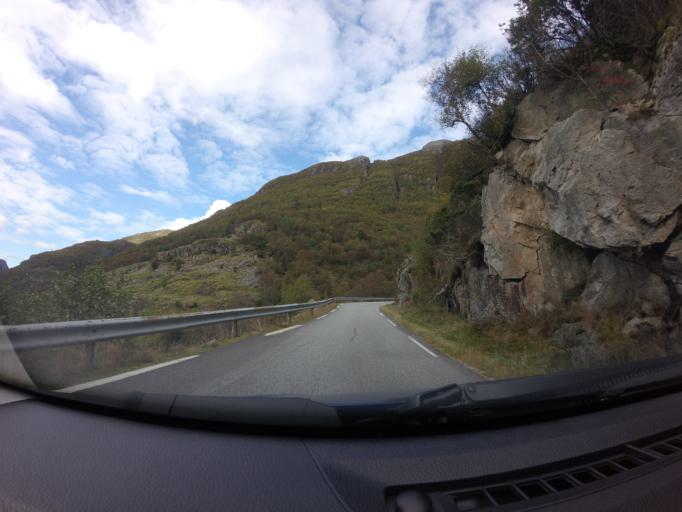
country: NO
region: Rogaland
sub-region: Forsand
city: Forsand
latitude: 58.8491
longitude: 6.3642
